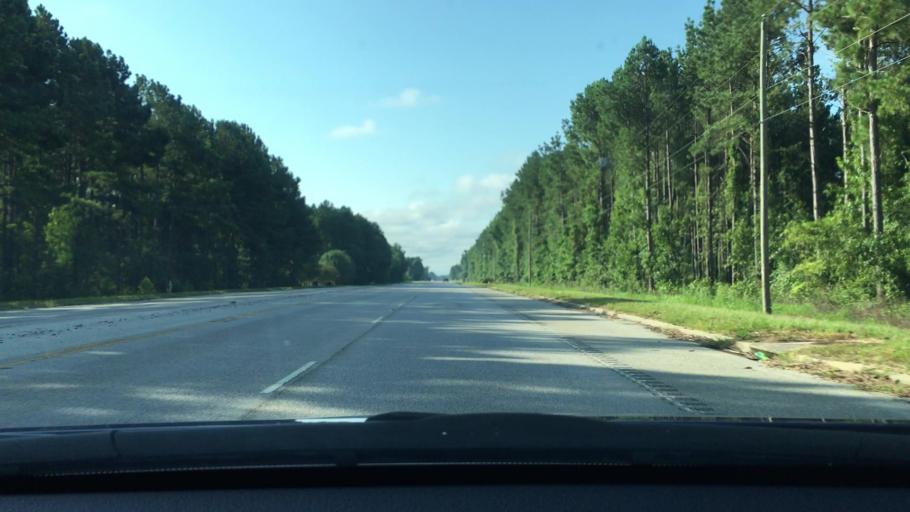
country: US
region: South Carolina
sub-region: Clarendon County
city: Manning
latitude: 33.7726
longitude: -80.2380
